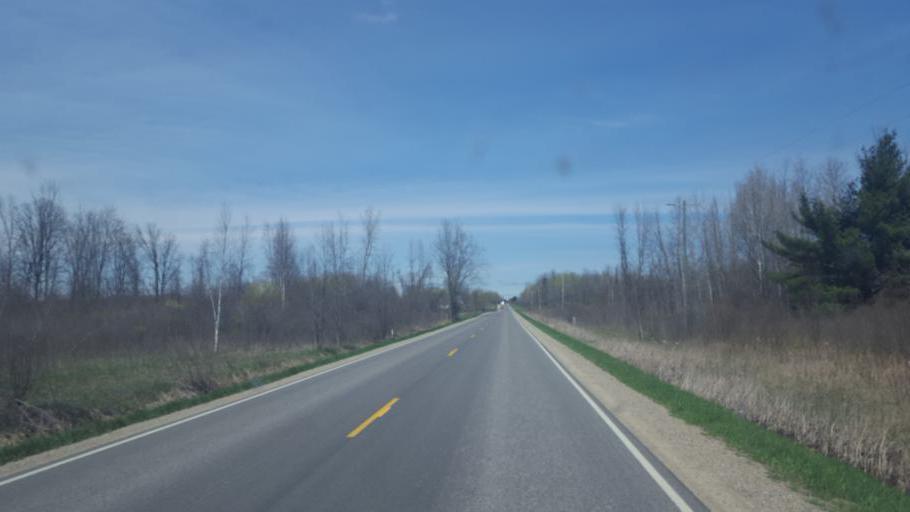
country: US
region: Michigan
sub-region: Gladwin County
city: Beaverton
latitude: 43.8933
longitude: -84.5855
